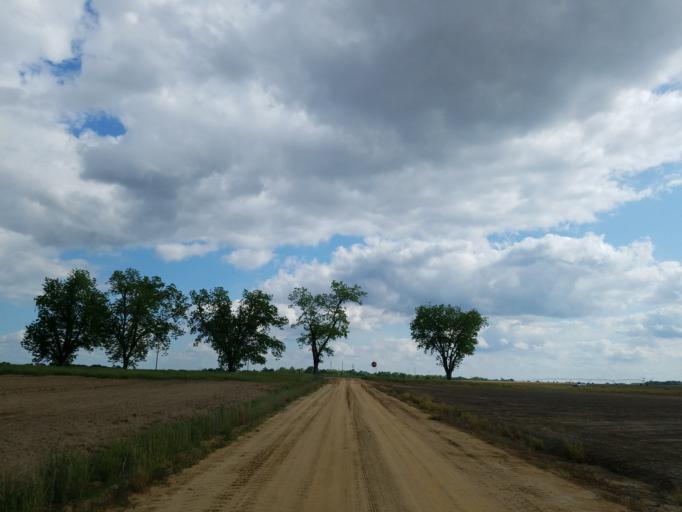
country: US
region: Georgia
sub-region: Dooly County
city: Vienna
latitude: 32.1672
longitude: -83.7759
